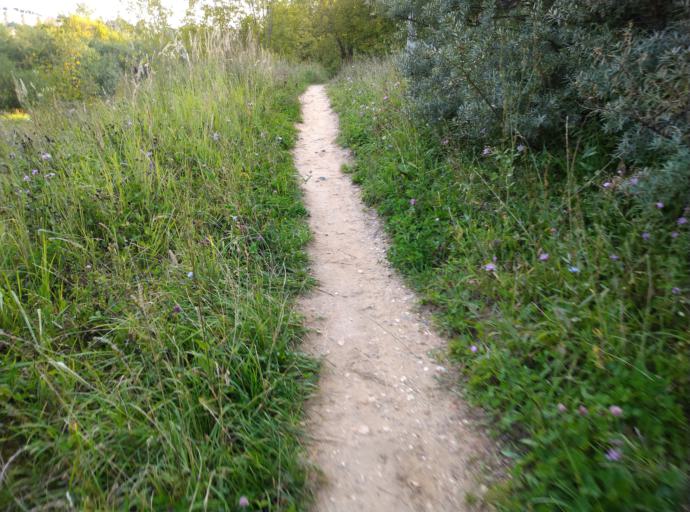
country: RU
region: Kostroma
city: Oktyabr'skiy
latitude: 57.7518
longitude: 40.9634
